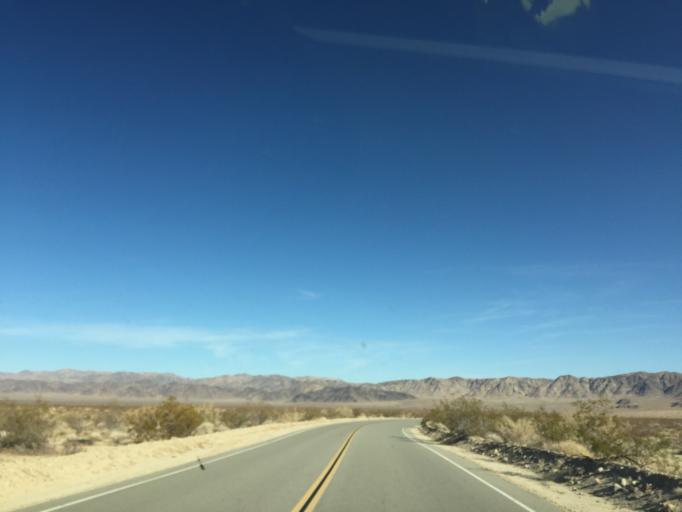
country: US
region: California
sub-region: San Bernardino County
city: Twentynine Palms
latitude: 33.8972
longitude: -115.8316
